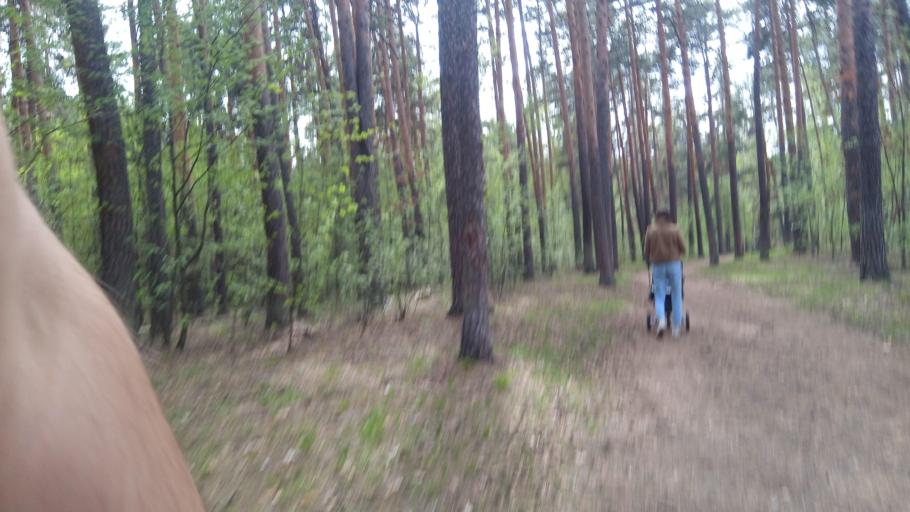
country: RU
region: Chelyabinsk
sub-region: Gorod Chelyabinsk
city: Chelyabinsk
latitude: 55.1534
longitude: 61.3529
